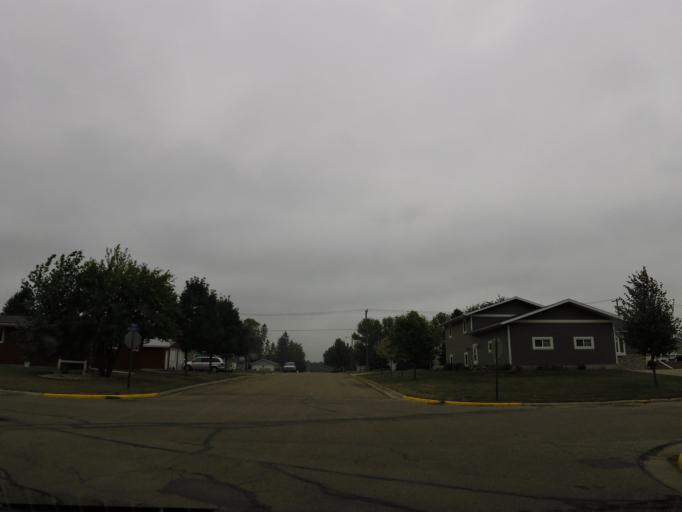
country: US
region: Minnesota
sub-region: Marshall County
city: Warren
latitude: 48.3338
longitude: -96.8242
